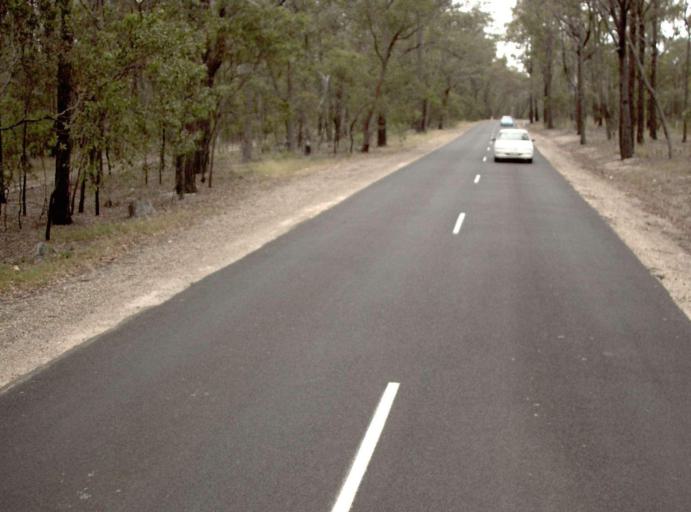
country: AU
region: Victoria
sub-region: Wellington
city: Heyfield
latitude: -37.9475
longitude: 146.7665
